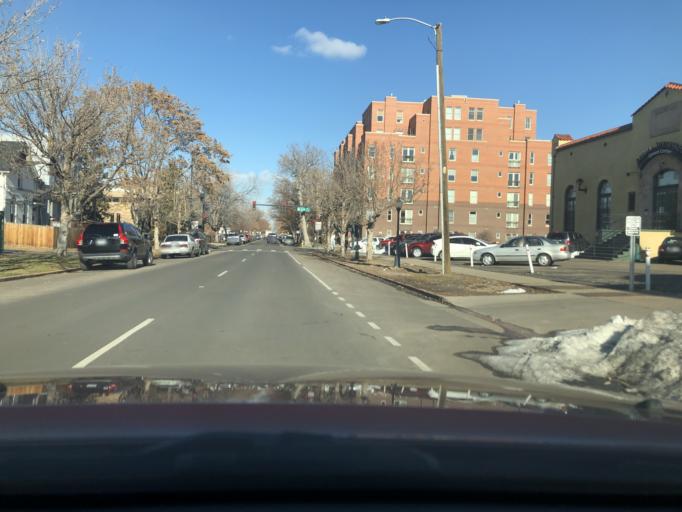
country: US
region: Colorado
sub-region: Denver County
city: Denver
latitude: 39.7410
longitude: -104.9775
